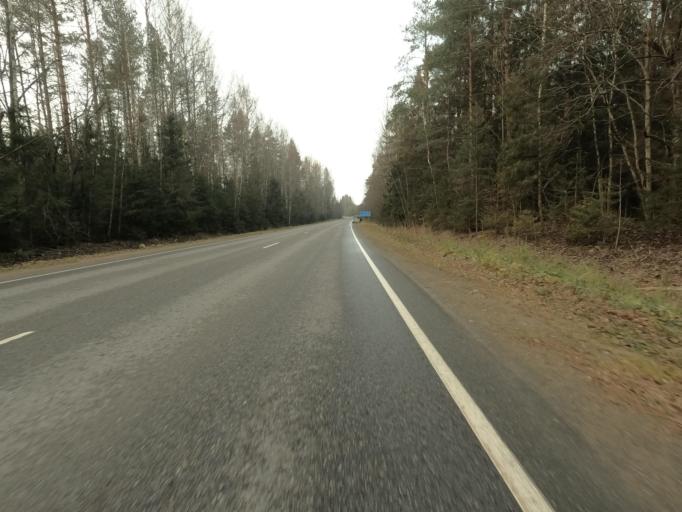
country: RU
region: Leningrad
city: Kirovsk
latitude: 59.8230
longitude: 30.9816
